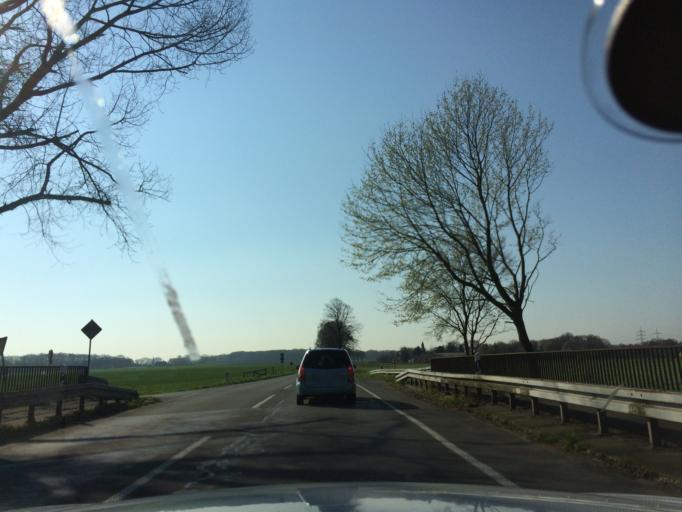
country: DE
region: North Rhine-Westphalia
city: Marl
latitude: 51.6365
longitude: 7.0824
